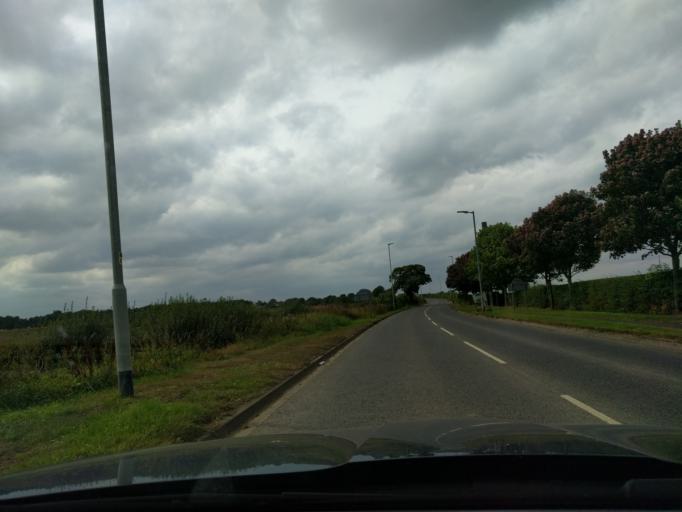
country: GB
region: England
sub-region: Northumberland
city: Choppington
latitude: 55.1332
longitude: -1.6202
